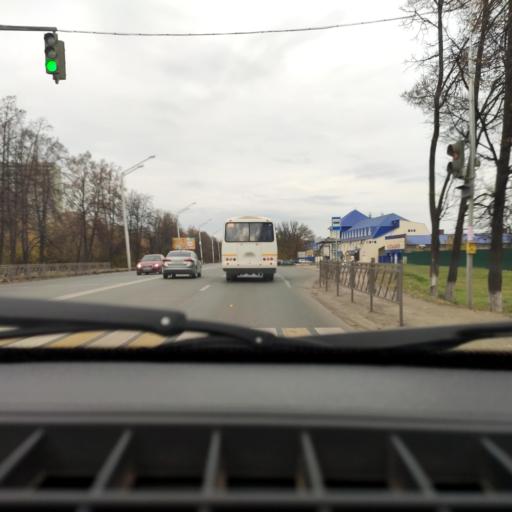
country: RU
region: Bashkortostan
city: Avdon
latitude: 54.6931
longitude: 55.8226
